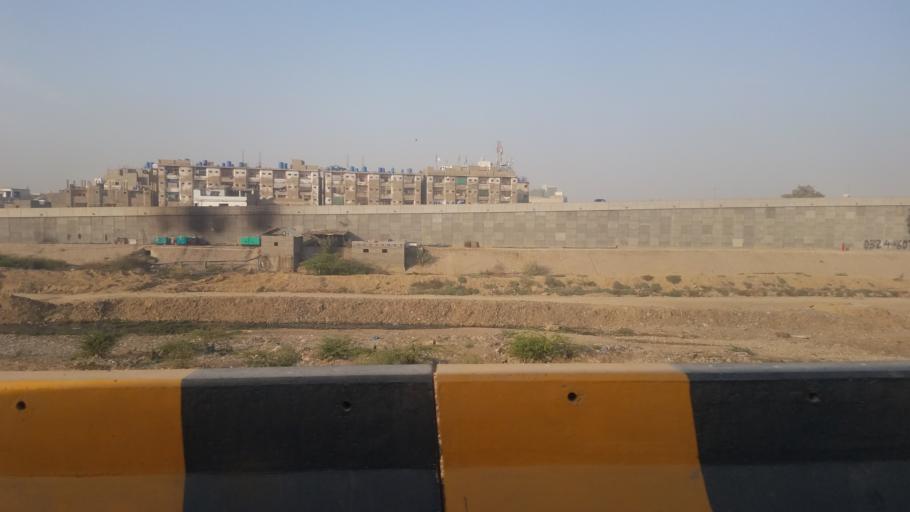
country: PK
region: Sindh
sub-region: Karachi District
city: Karachi
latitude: 24.9439
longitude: 67.0889
